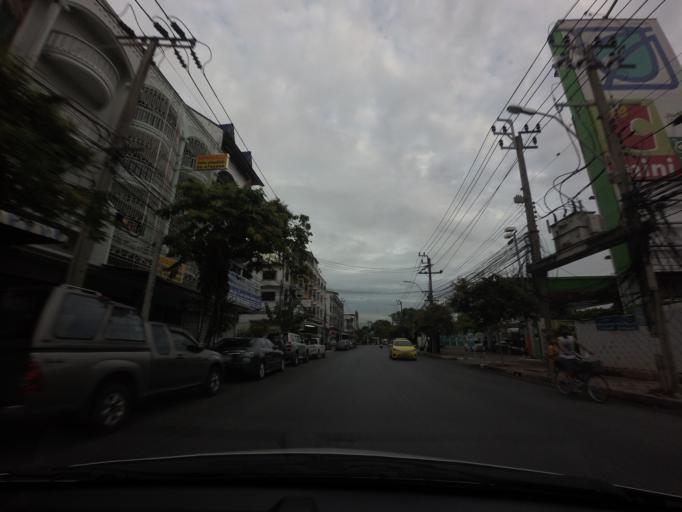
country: TH
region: Bangkok
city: Chom Thong
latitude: 13.6836
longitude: 100.4645
